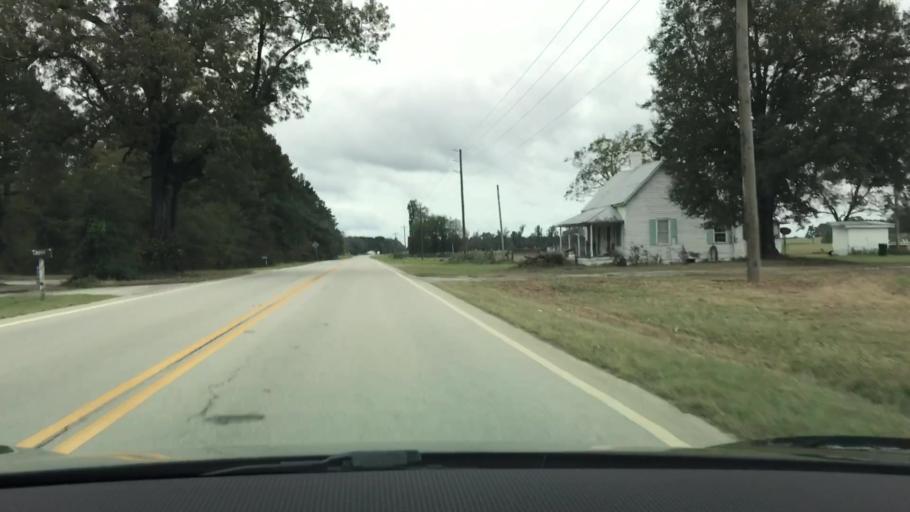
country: US
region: Georgia
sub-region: Jefferson County
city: Wrens
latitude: 33.1774
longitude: -82.4534
